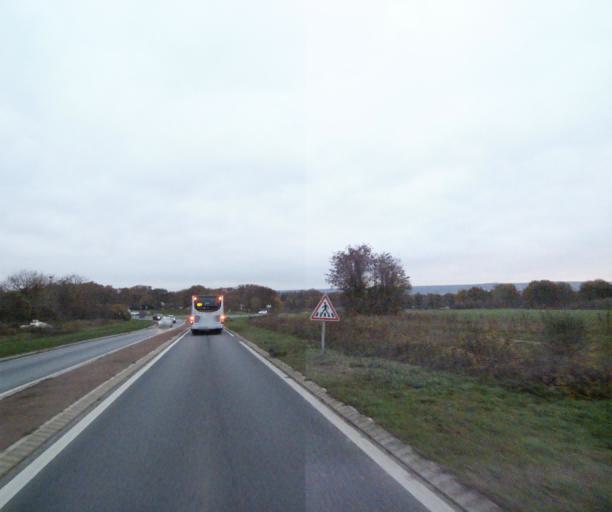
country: FR
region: Ile-de-France
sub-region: Departement des Yvelines
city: Vernouillet
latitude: 48.9577
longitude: 1.9800
